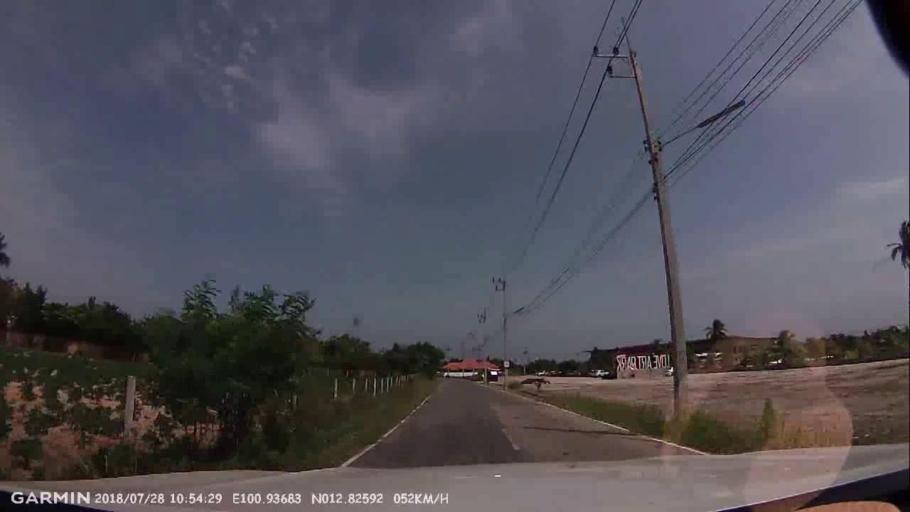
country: TH
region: Chon Buri
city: Phatthaya
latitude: 12.8260
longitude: 100.9367
